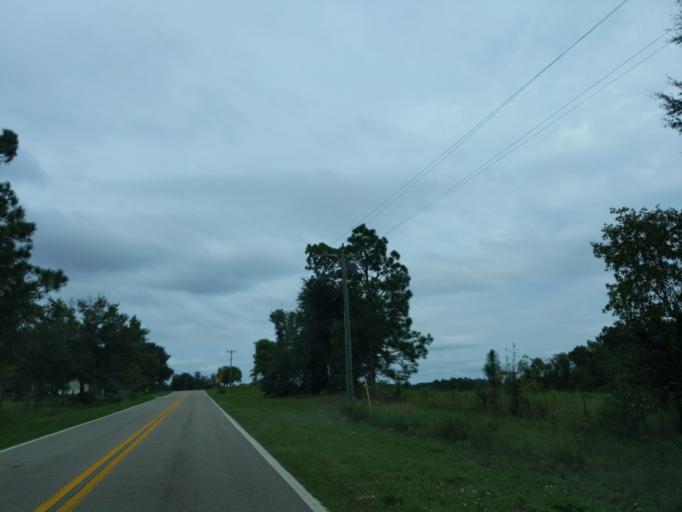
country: US
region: Florida
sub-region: Gadsden County
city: Midway
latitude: 30.4343
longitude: -84.4122
